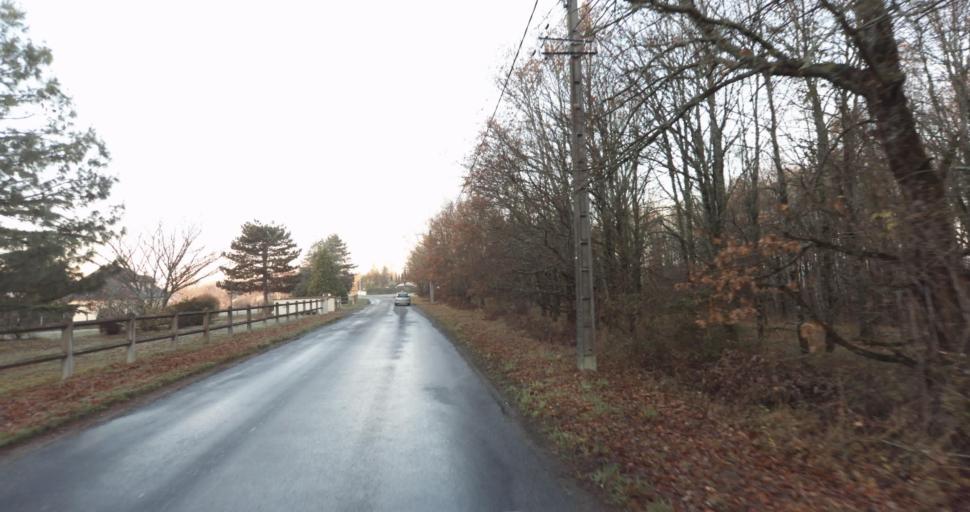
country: FR
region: Limousin
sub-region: Departement de la Haute-Vienne
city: Aixe-sur-Vienne
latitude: 45.8153
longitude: 1.1571
